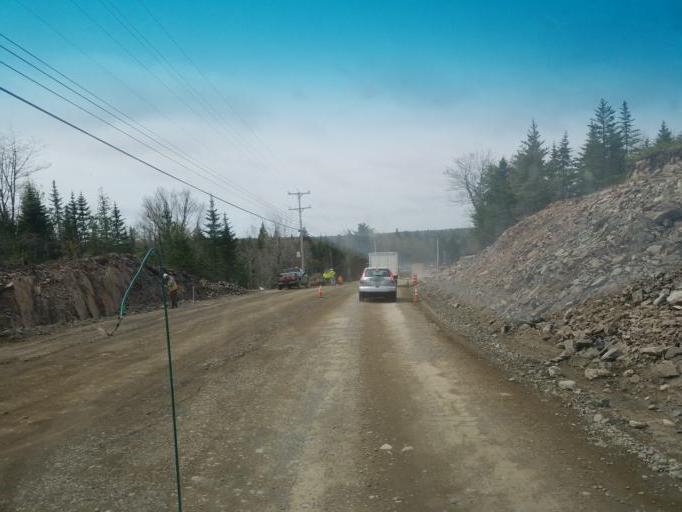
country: US
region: Maine
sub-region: Washington County
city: East Machias
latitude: 44.7688
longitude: -67.1977
